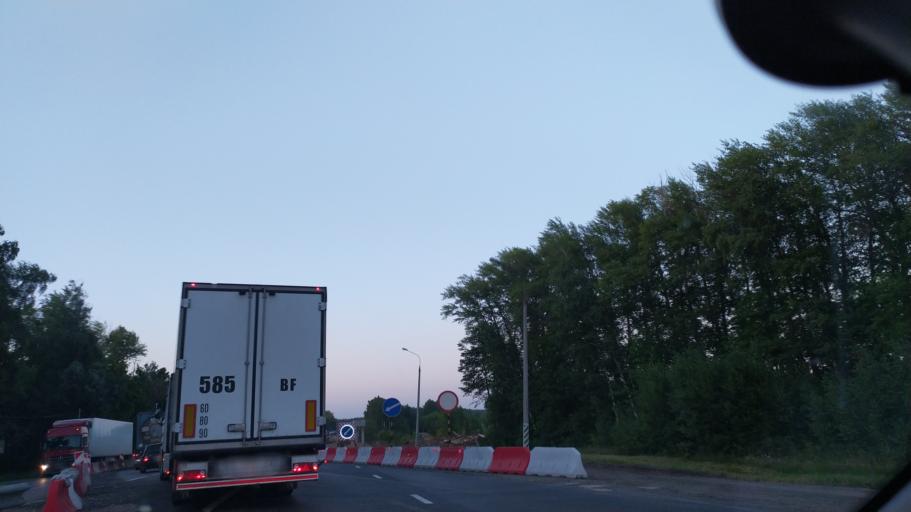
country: RU
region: Chuvashia
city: Ishley
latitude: 56.1035
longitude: 47.0388
